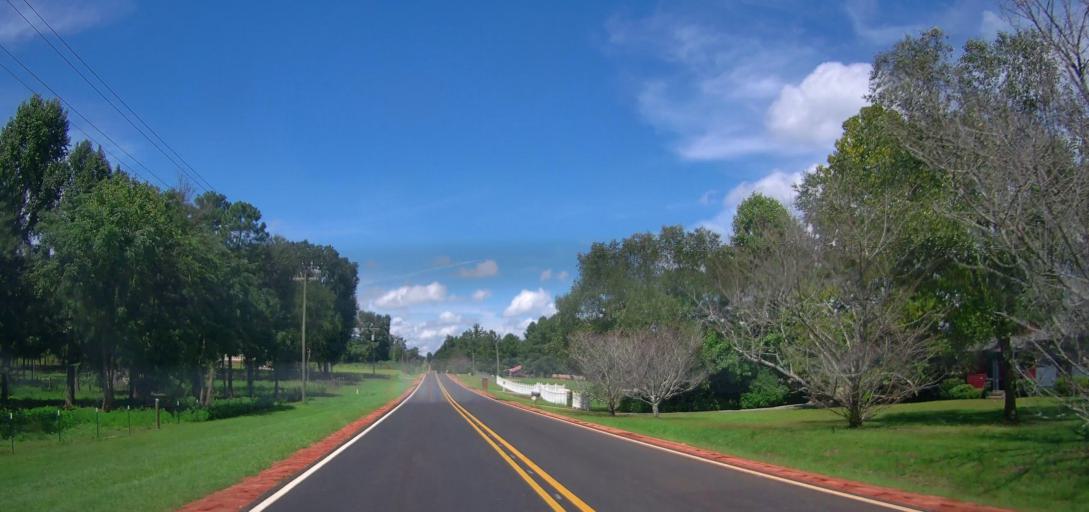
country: US
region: Georgia
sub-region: Peach County
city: Fort Valley
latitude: 32.4847
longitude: -83.8649
